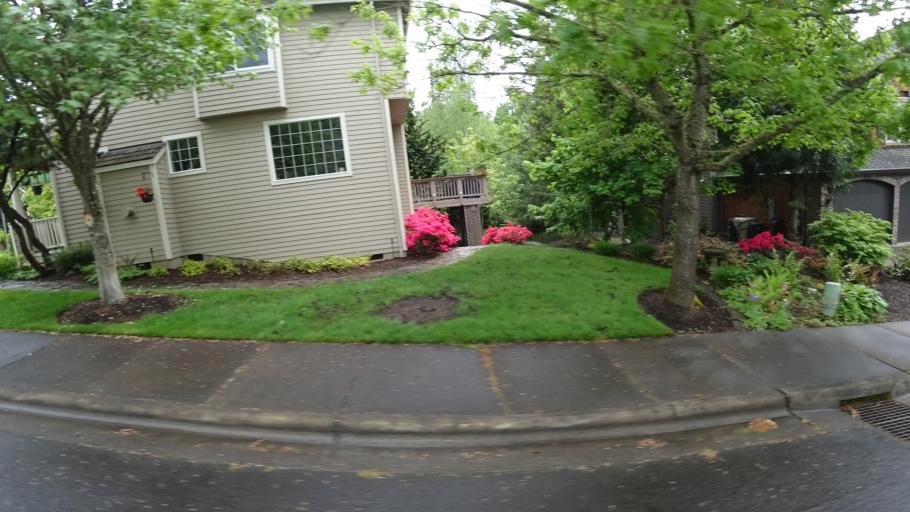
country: US
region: Oregon
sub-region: Washington County
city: West Haven
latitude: 45.5325
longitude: -122.7678
